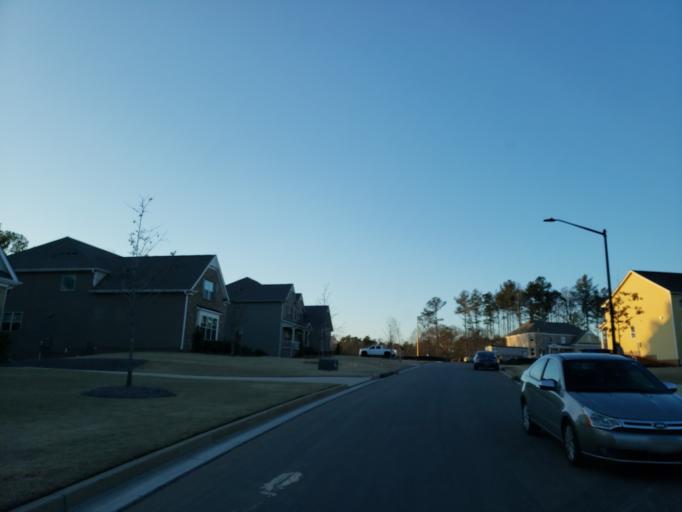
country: US
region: Georgia
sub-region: Cherokee County
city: Woodstock
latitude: 34.1159
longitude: -84.4545
